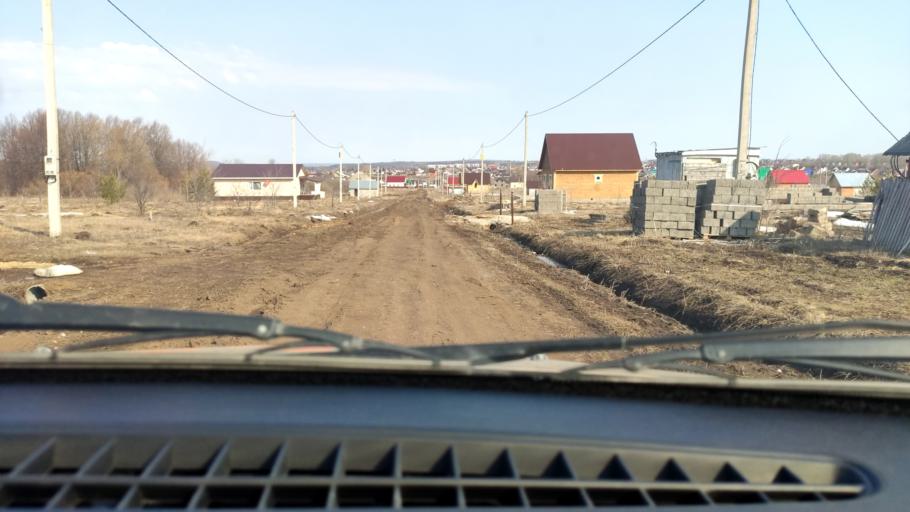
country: RU
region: Bashkortostan
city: Iglino
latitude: 54.7967
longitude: 56.4023
